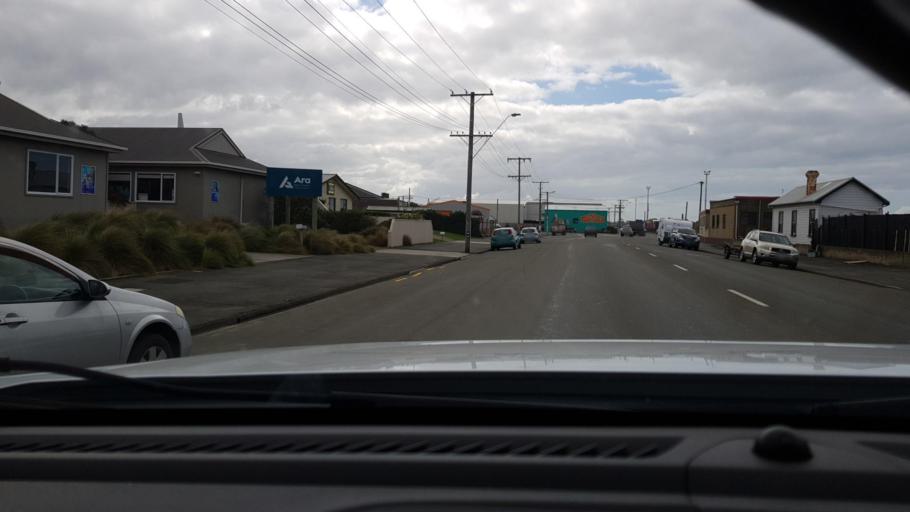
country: NZ
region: Otago
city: Oamaru
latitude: -45.0957
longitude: 170.9751
